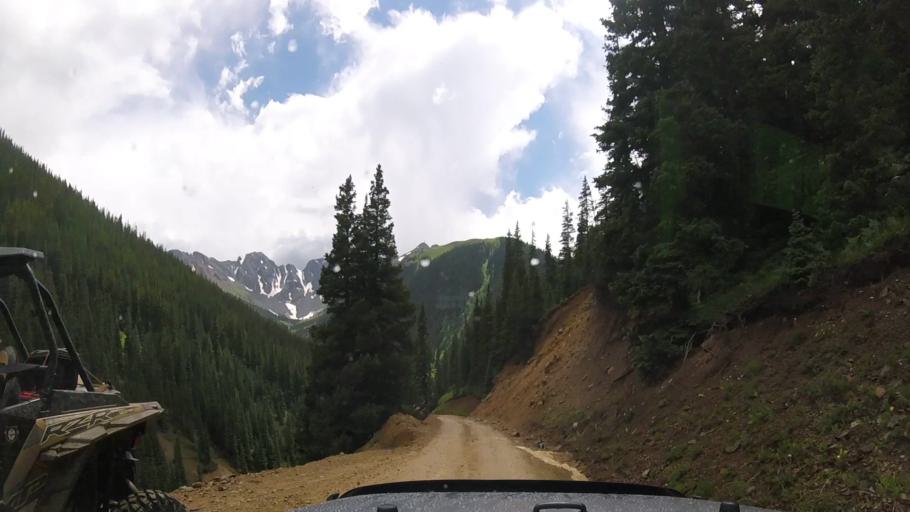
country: US
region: Colorado
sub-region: San Juan County
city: Silverton
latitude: 37.8945
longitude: -107.6482
